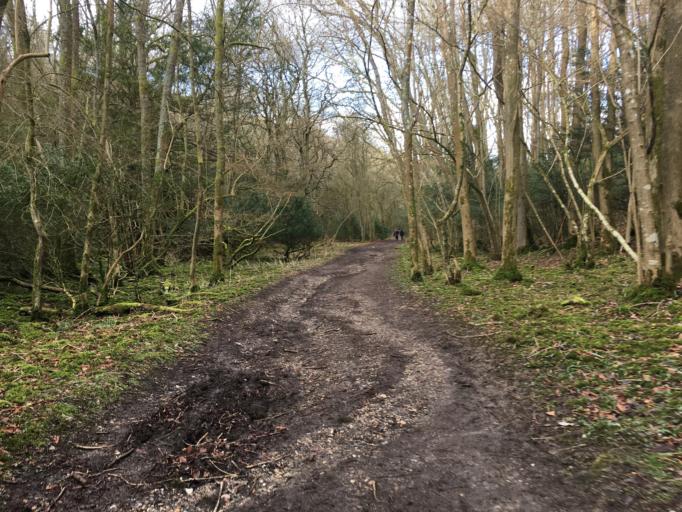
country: GB
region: England
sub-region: Surrey
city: Mickleham
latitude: 51.2529
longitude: -0.3063
